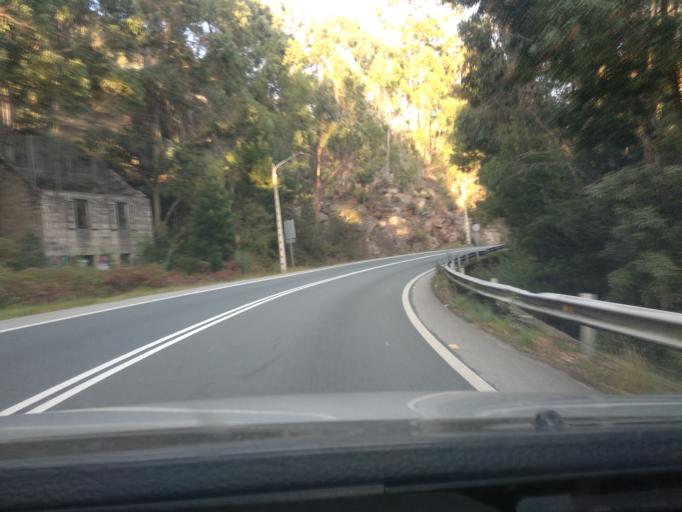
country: ES
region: Galicia
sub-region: Provincia de Pontevedra
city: Redondela
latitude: 42.2921
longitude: -8.6673
